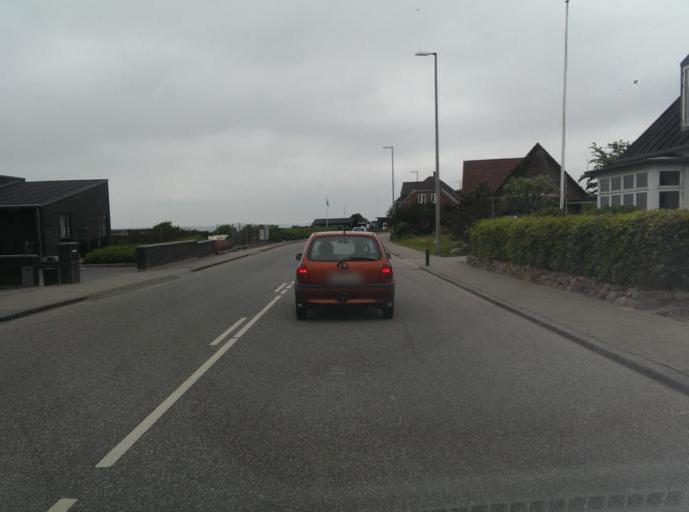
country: DK
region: South Denmark
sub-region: Fano Kommune
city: Nordby
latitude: 55.5210
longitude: 8.3583
